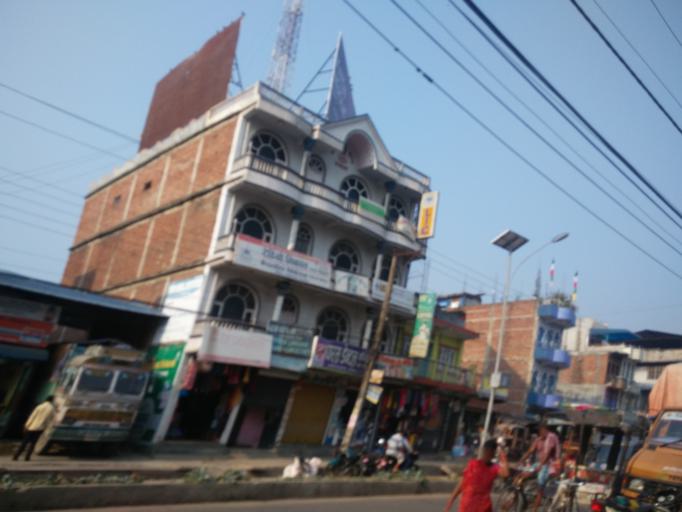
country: NP
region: Central Region
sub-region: Narayani Zone
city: Hitura
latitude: 27.4305
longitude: 85.0337
